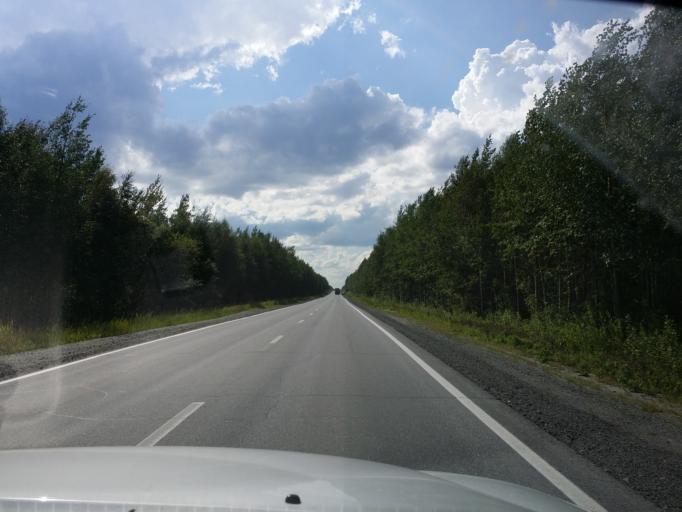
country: RU
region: Khanty-Mansiyskiy Avtonomnyy Okrug
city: Langepas
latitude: 61.1598
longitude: 75.6507
